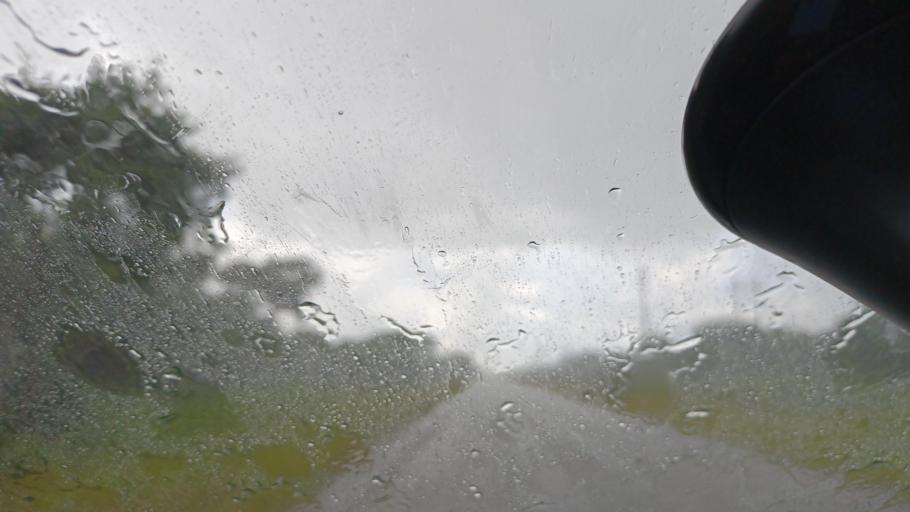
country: ZM
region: North-Western
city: Kasempa
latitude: -13.0946
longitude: 25.9161
